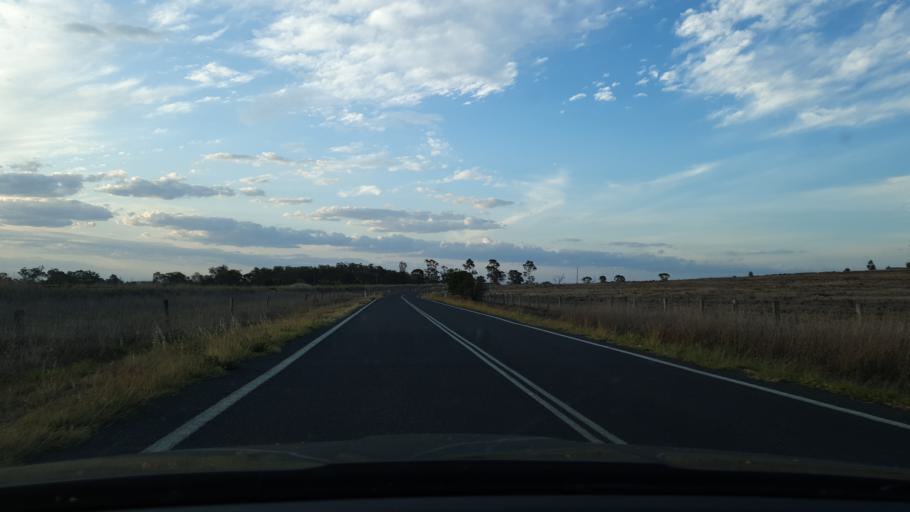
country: AU
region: Queensland
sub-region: Southern Downs
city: Warwick
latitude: -28.1801
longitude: 151.9766
